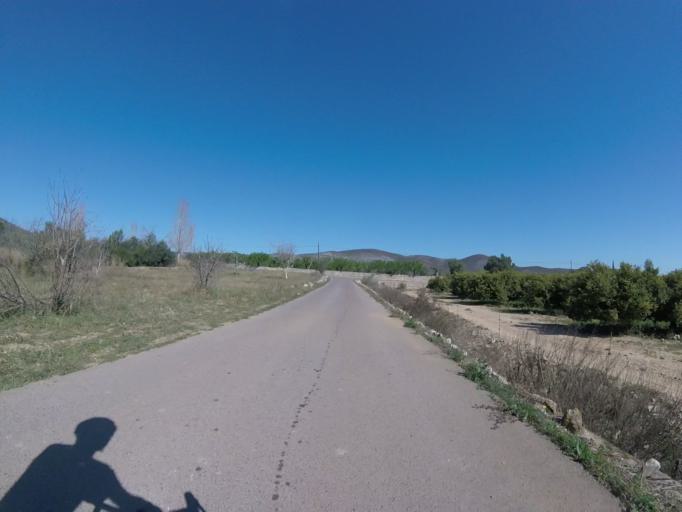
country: ES
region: Valencia
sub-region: Provincia de Castello
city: Santa Magdalena de Pulpis
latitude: 40.3595
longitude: 0.2858
